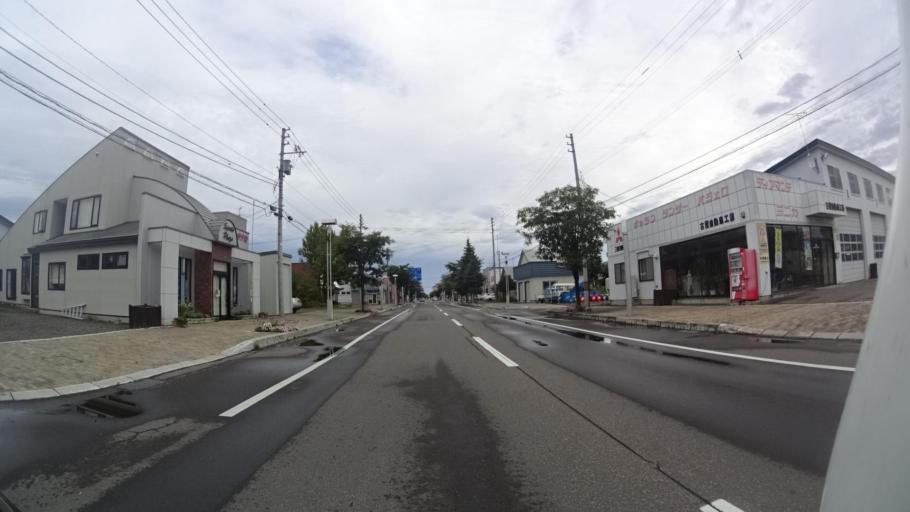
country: JP
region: Hokkaido
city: Abashiri
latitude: 43.8358
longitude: 144.5960
